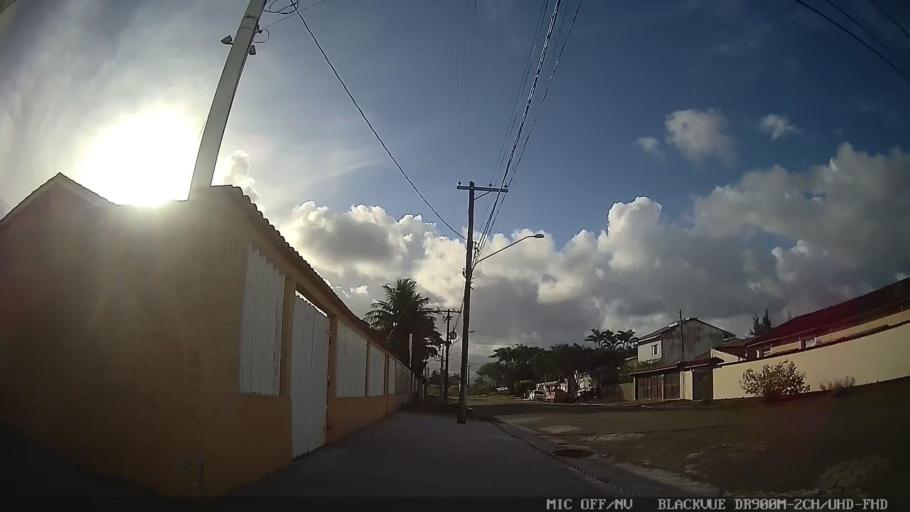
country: BR
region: Sao Paulo
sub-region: Itanhaem
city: Itanhaem
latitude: -24.2087
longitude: -46.8372
